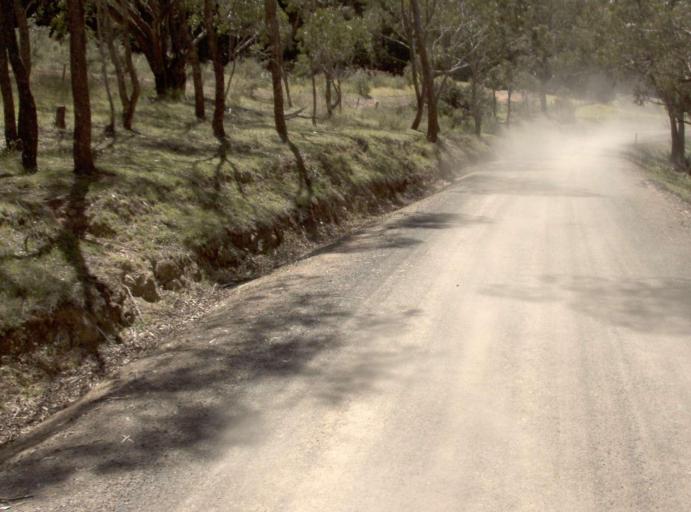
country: AU
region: New South Wales
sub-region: Bombala
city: Bombala
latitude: -37.1231
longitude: 148.6624
